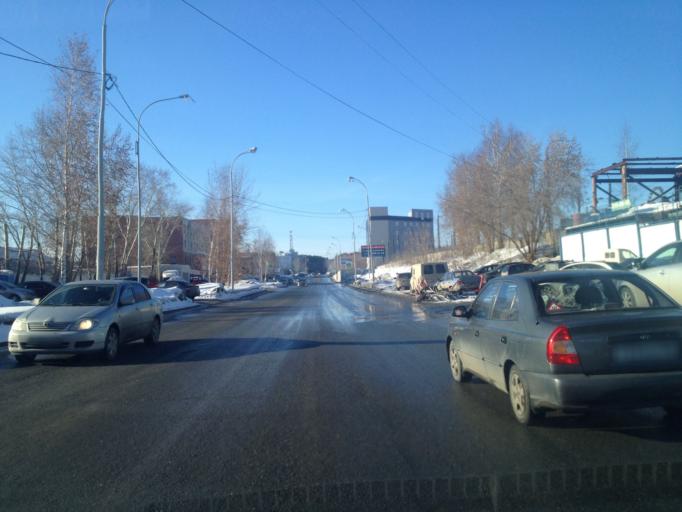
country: RU
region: Sverdlovsk
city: Sovkhoznyy
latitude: 56.8106
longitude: 60.5450
